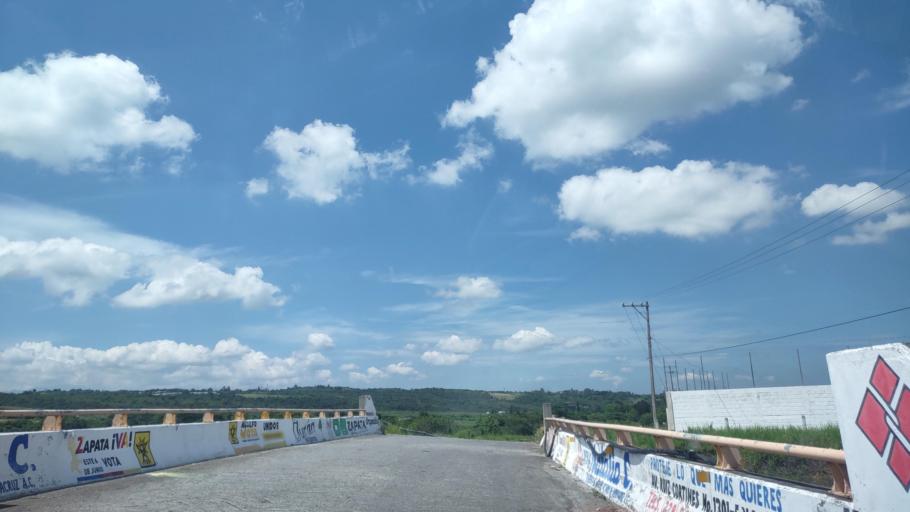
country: MX
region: Veracruz
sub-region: Emiliano Zapata
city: Dos Rios
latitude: 19.4968
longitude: -96.8034
